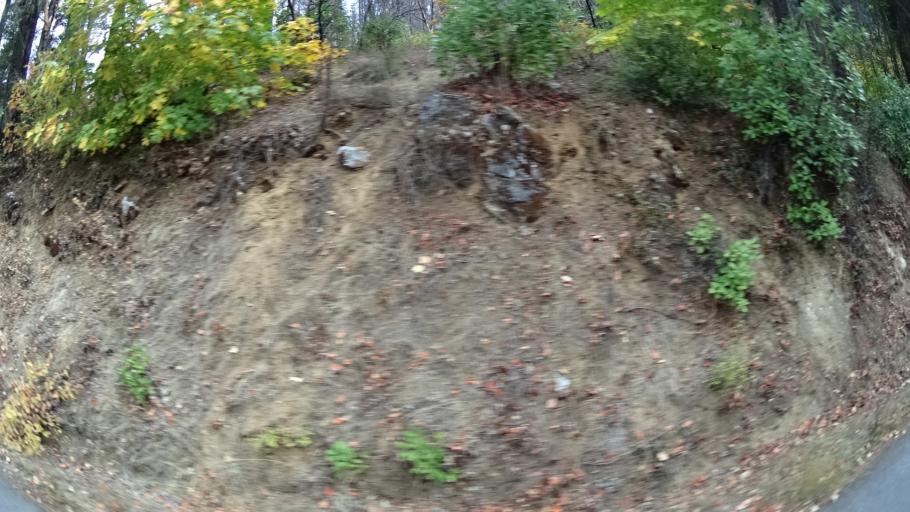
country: US
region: California
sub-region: Siskiyou County
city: Happy Camp
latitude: 41.7869
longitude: -123.3043
